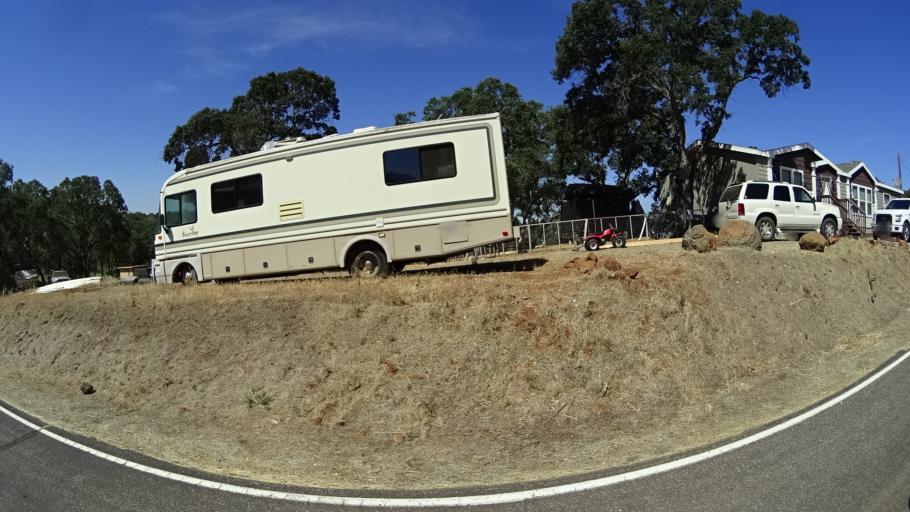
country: US
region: California
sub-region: Calaveras County
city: Rancho Calaveras
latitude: 38.1461
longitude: -120.8533
